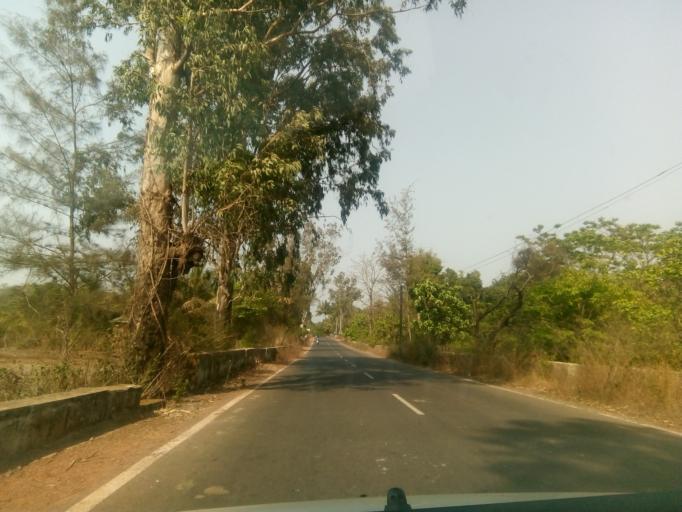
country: IN
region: Goa
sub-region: North Goa
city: Pernem
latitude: 15.6932
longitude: 73.8424
